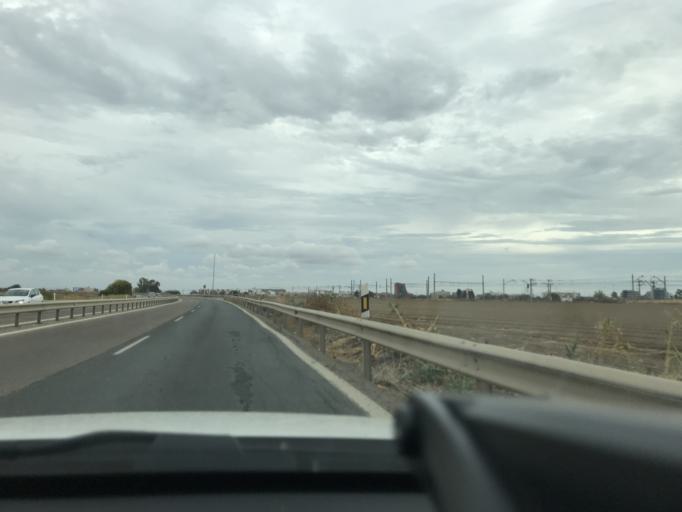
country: ES
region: Andalusia
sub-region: Provincia de Sevilla
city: Sevilla
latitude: 37.4211
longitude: -5.9469
